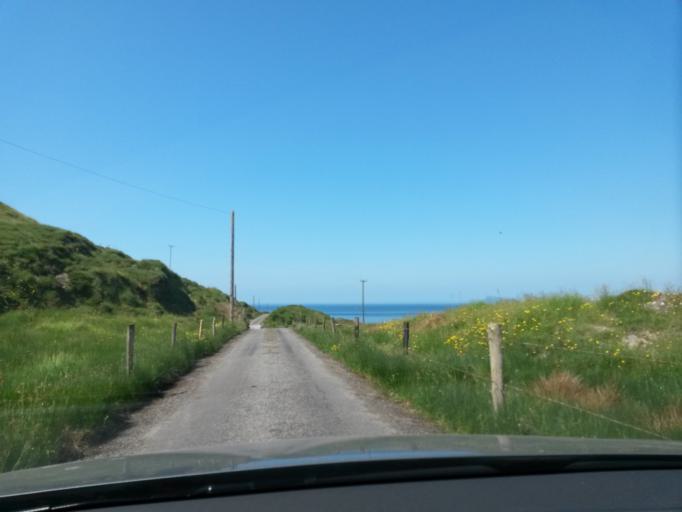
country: IE
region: Munster
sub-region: Ciarrai
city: Cahersiveen
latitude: 51.7304
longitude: -9.9717
